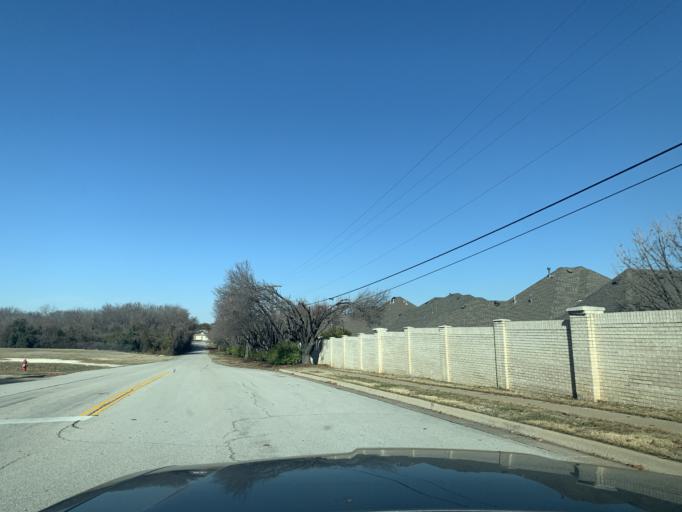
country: US
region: Texas
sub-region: Tarrant County
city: Bedford
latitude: 32.8416
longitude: -97.1373
